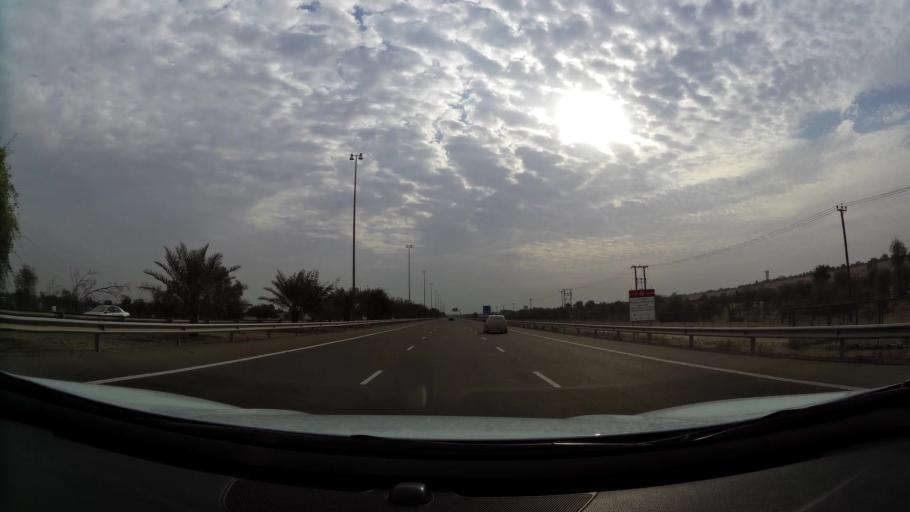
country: AE
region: Abu Dhabi
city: Al Ain
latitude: 24.1690
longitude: 55.0801
